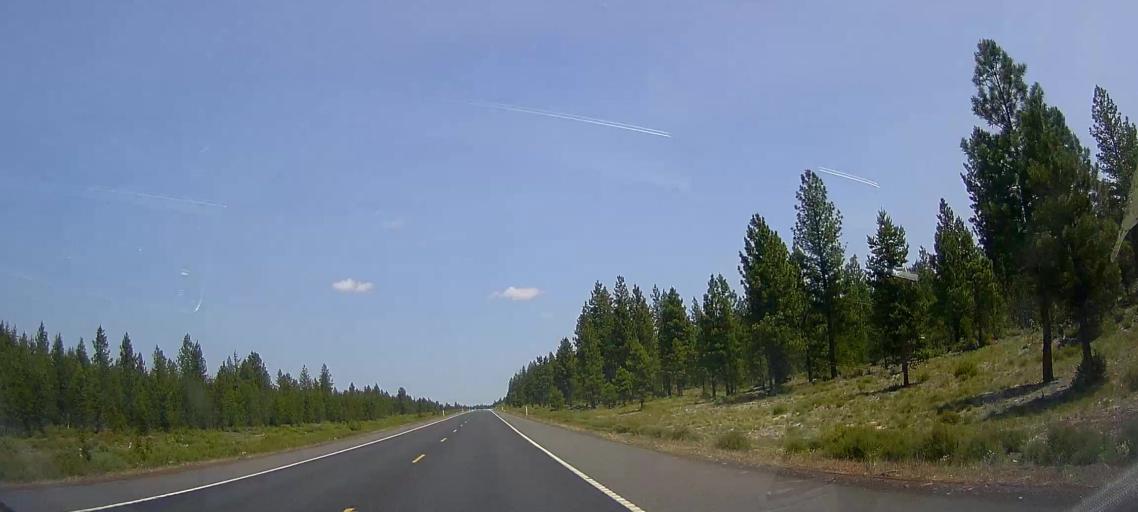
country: US
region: Oregon
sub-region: Deschutes County
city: La Pine
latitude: 43.5102
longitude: -121.6587
